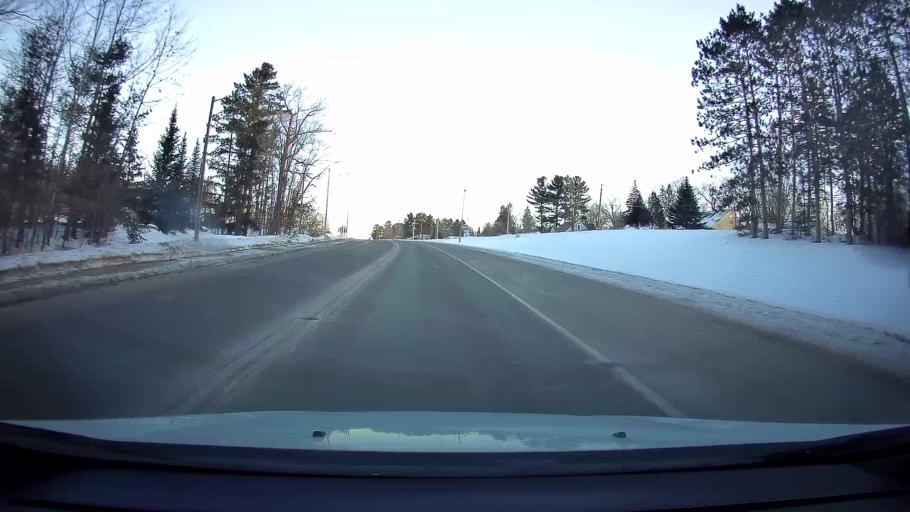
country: US
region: Wisconsin
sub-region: Barron County
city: Cumberland
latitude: 45.5453
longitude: -92.0174
